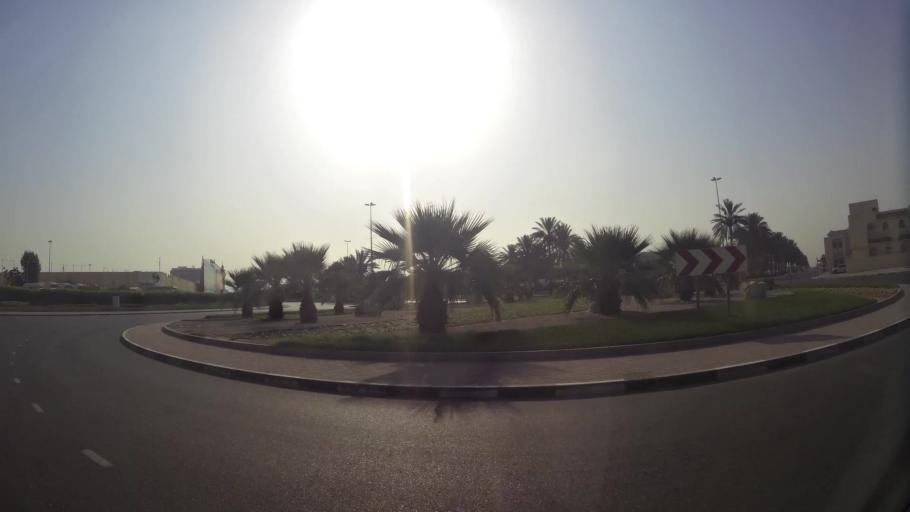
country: AE
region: Ash Shariqah
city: Sharjah
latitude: 25.2926
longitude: 55.3273
